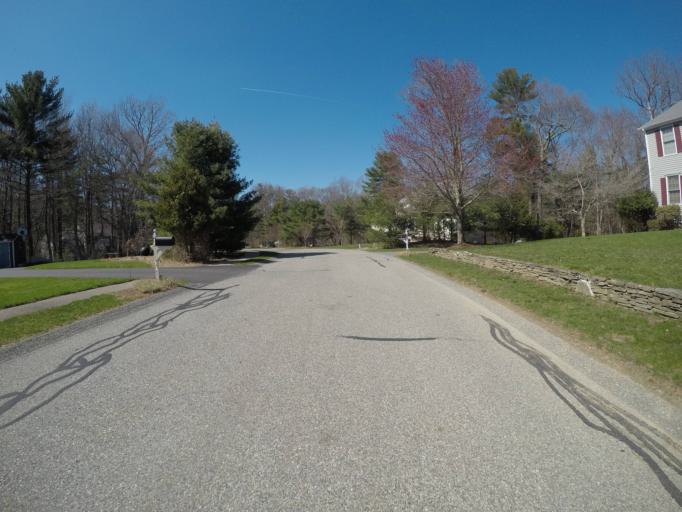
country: US
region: Massachusetts
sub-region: Norfolk County
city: Stoughton
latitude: 42.0812
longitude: -71.0936
